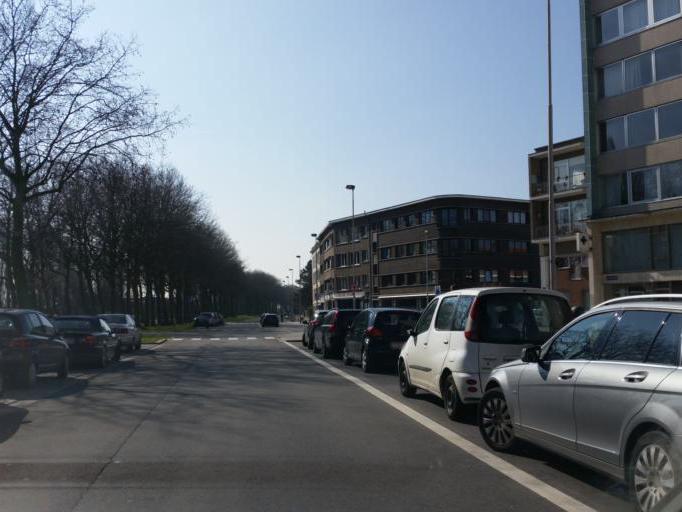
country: BE
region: Flanders
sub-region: Provincie Antwerpen
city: Antwerpen
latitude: 51.2198
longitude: 4.3867
